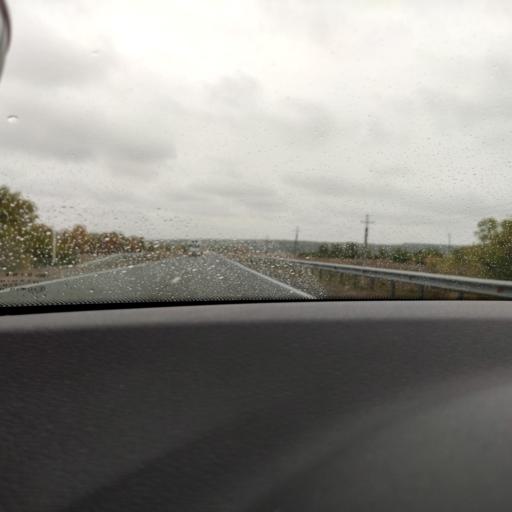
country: RU
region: Samara
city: Mirnyy
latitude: 53.6251
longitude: 50.2496
